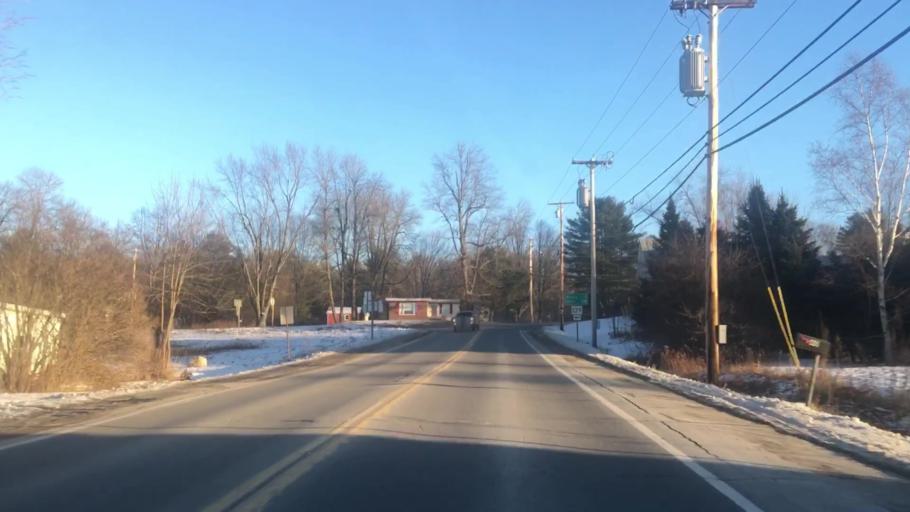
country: US
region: Maine
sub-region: Kennebec County
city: Benton
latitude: 44.5850
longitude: -69.5481
